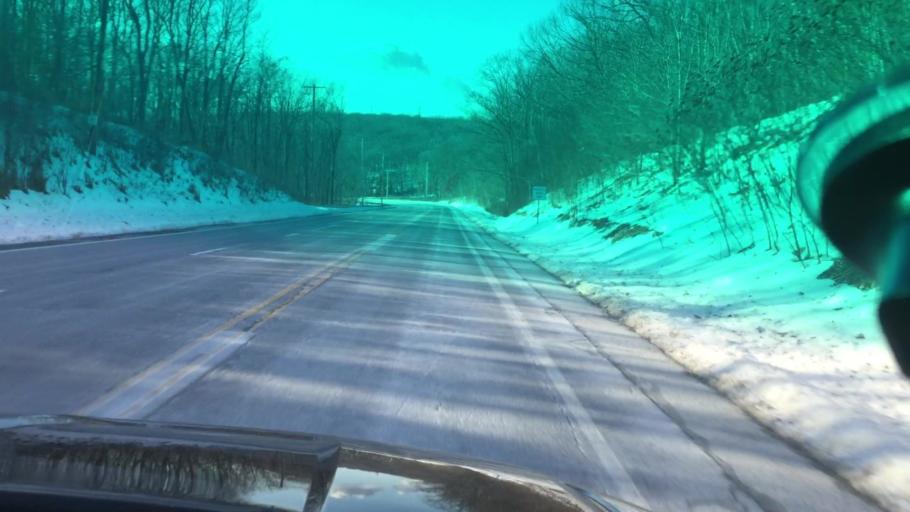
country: US
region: Pennsylvania
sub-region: Luzerne County
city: Oakdale
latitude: 41.0184
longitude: -75.9294
